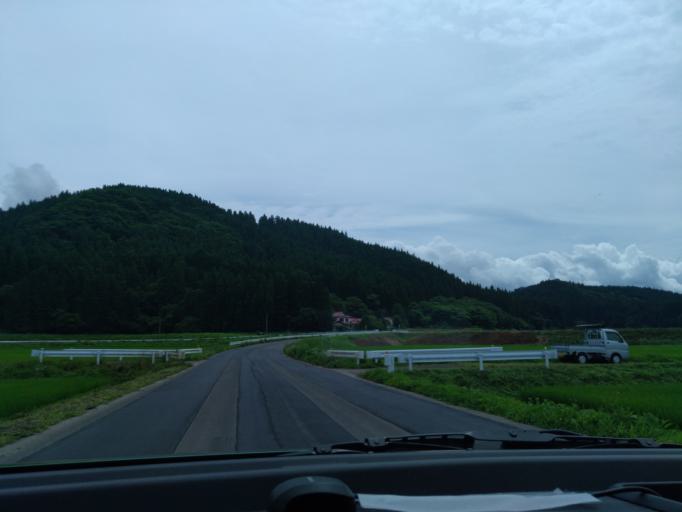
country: JP
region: Akita
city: Kakunodatemachi
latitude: 39.5957
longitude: 140.6168
